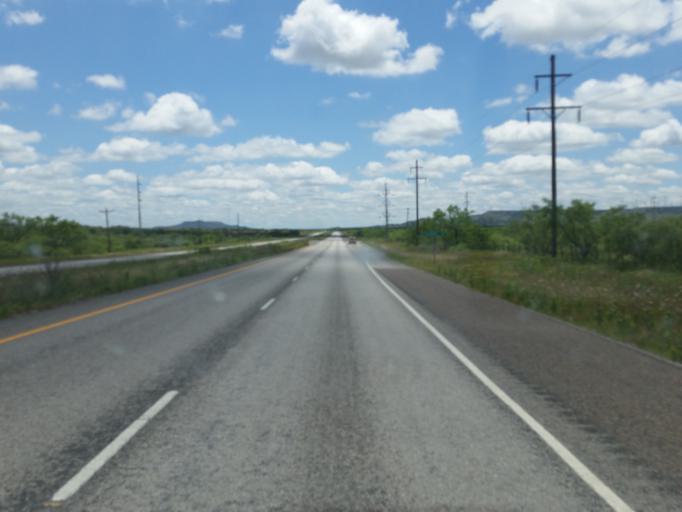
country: US
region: Texas
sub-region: Garza County
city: Post
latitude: 32.9973
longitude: -101.1537
